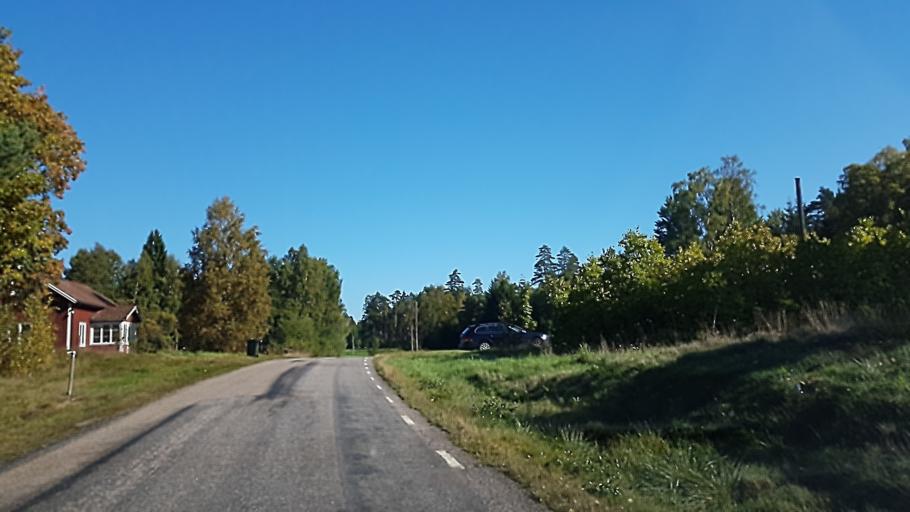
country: SE
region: Kronoberg
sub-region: Ljungby Kommun
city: Ljungby
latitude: 56.8114
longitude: 14.0343
